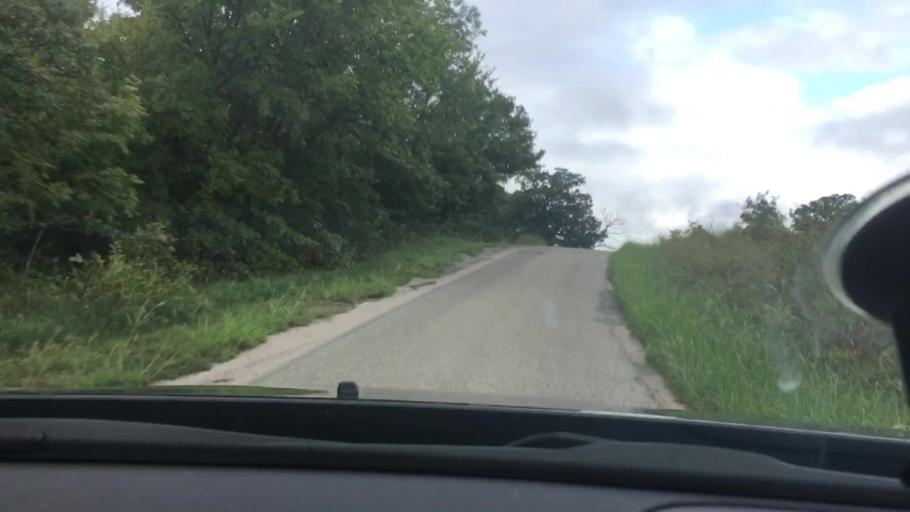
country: US
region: Oklahoma
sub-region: Pontotoc County
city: Byng
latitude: 34.8181
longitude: -96.5386
